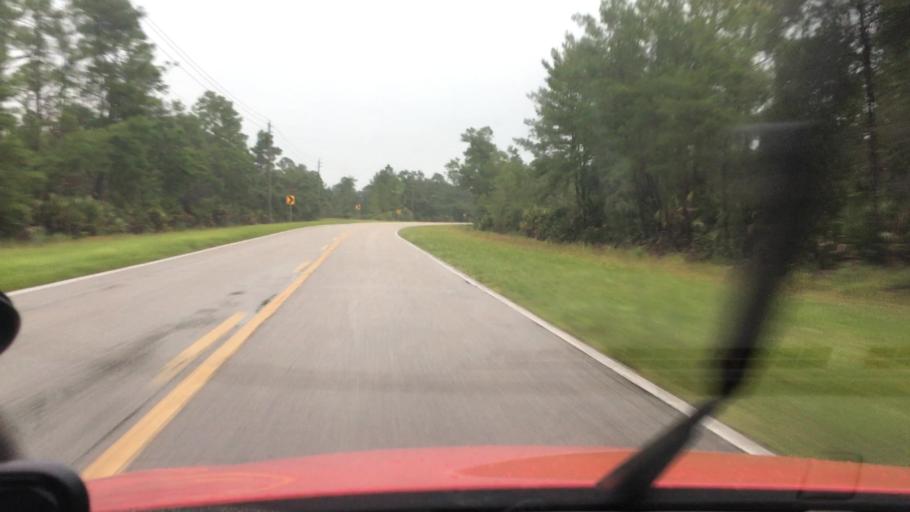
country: US
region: Florida
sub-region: Volusia County
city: Samsula-Spruce Creek
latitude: 29.0356
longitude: -81.0865
